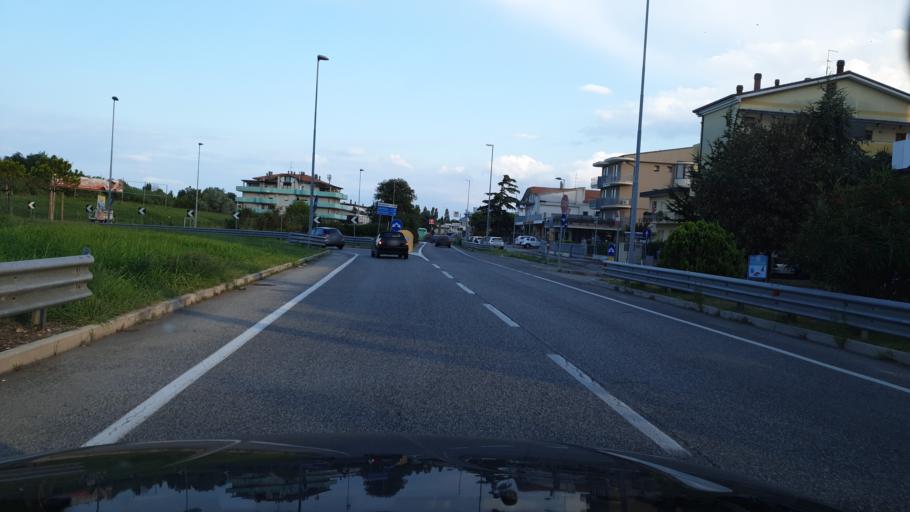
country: IT
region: Emilia-Romagna
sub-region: Provincia di Rimini
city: Rivazzurra
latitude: 44.0316
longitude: 12.6068
